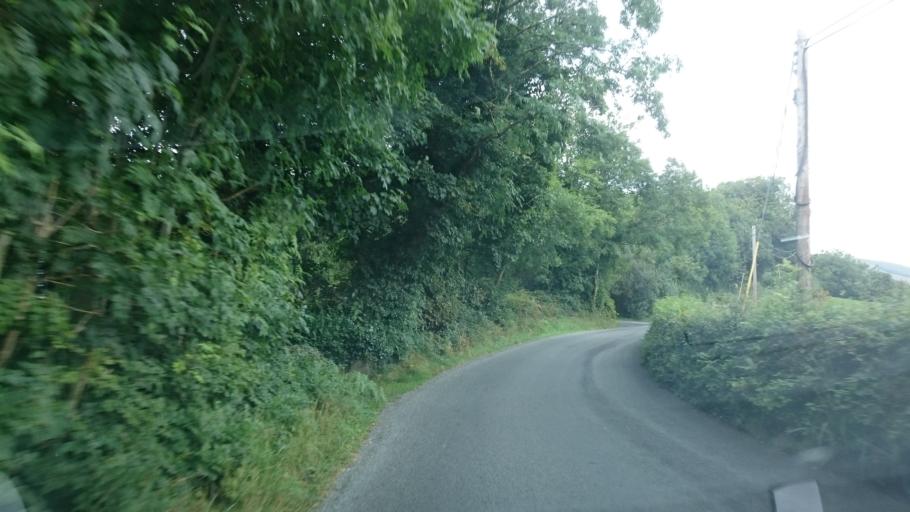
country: IE
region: Connaught
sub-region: Maigh Eo
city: Westport
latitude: 53.9041
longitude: -9.5506
